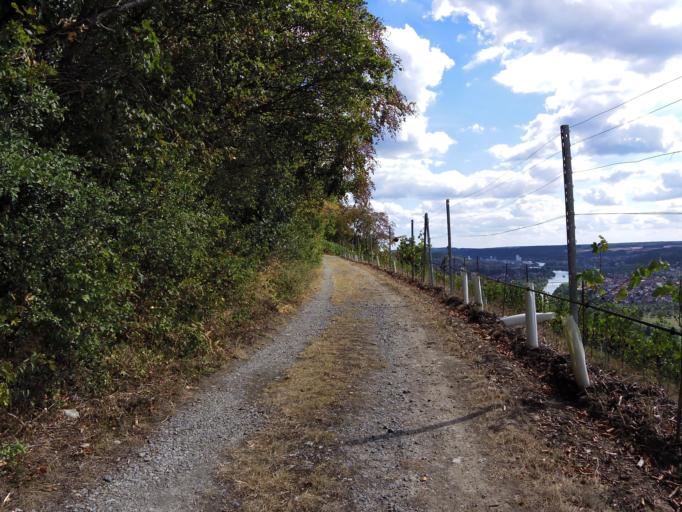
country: DE
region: Bavaria
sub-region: Regierungsbezirk Unterfranken
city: Margetshochheim
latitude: 49.8553
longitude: 9.8645
